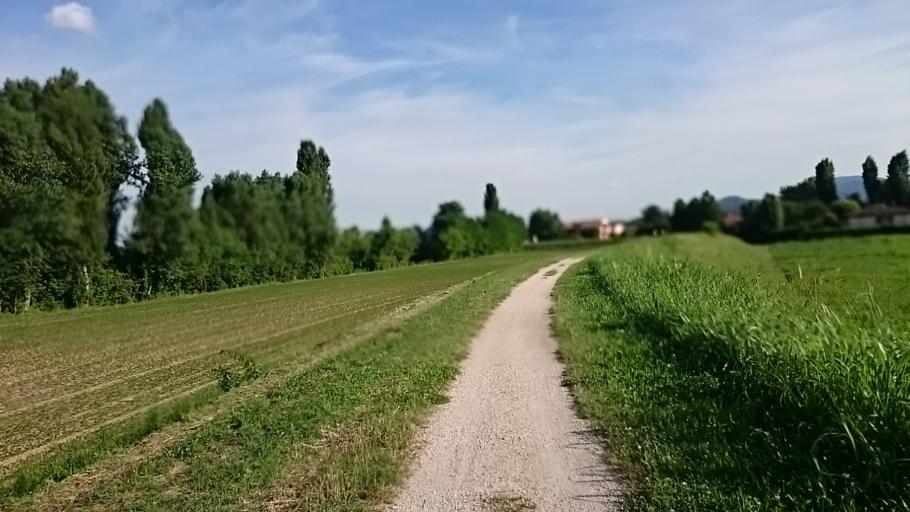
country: IT
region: Veneto
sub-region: Provincia di Padova
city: Saccolongo
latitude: 45.4108
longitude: 11.7426
